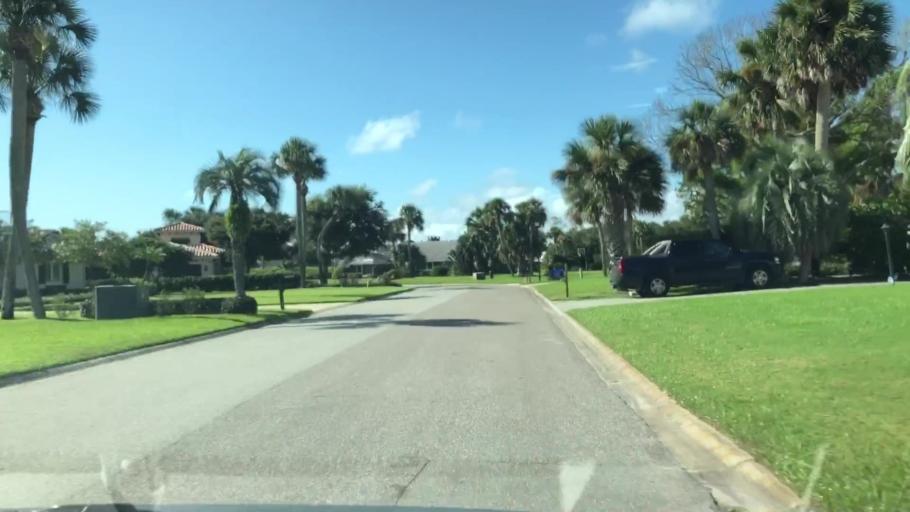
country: US
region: Florida
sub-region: Saint Johns County
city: Ponte Vedra Beach
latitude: 30.2344
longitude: -81.3837
